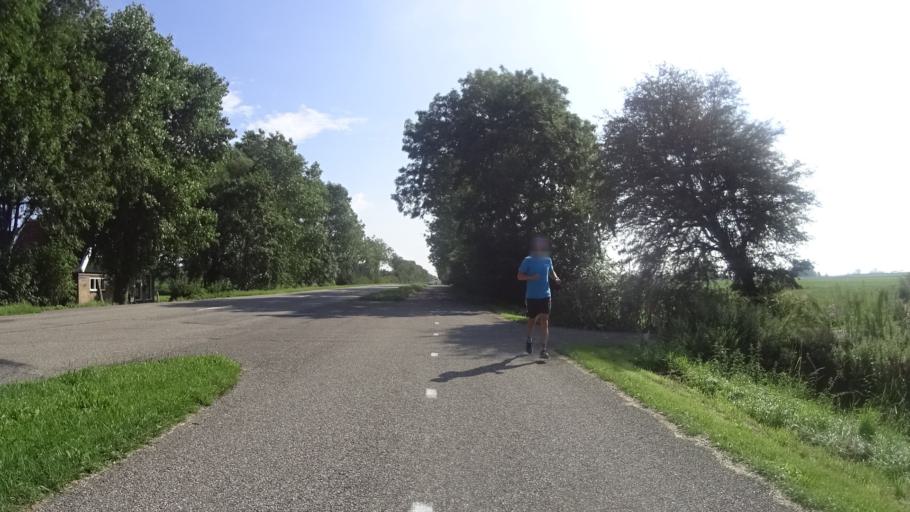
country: NL
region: Friesland
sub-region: Menameradiel
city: Dronryp
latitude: 53.1950
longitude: 5.6111
